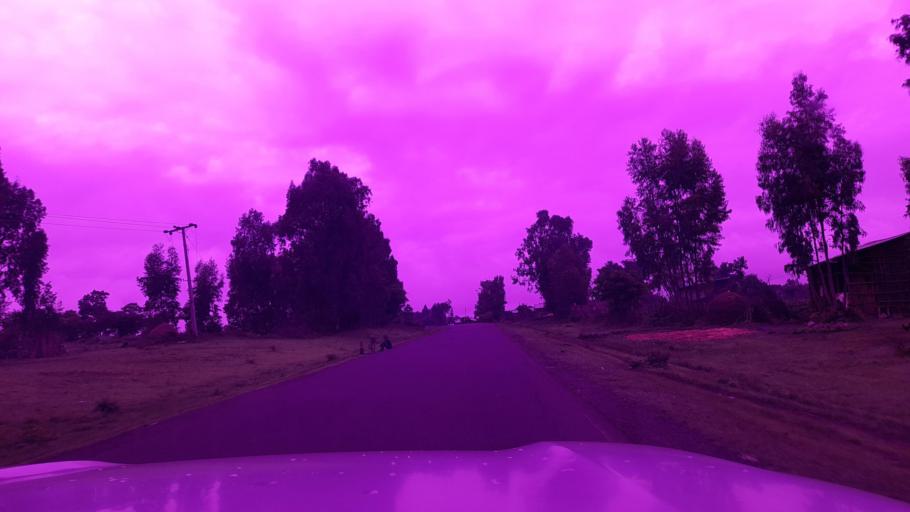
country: ET
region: Oromiya
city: Waliso
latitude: 8.2753
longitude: 37.6801
